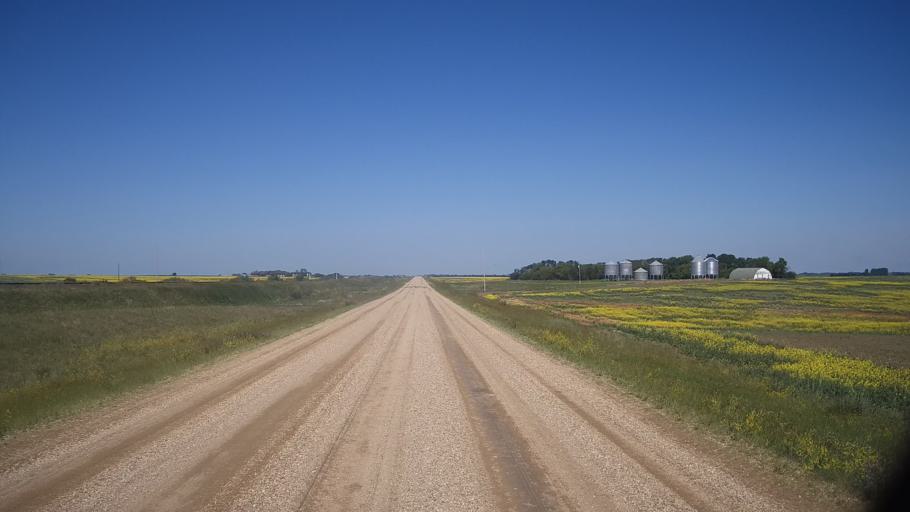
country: CA
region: Saskatchewan
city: Watrous
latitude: 51.8619
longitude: -105.9672
